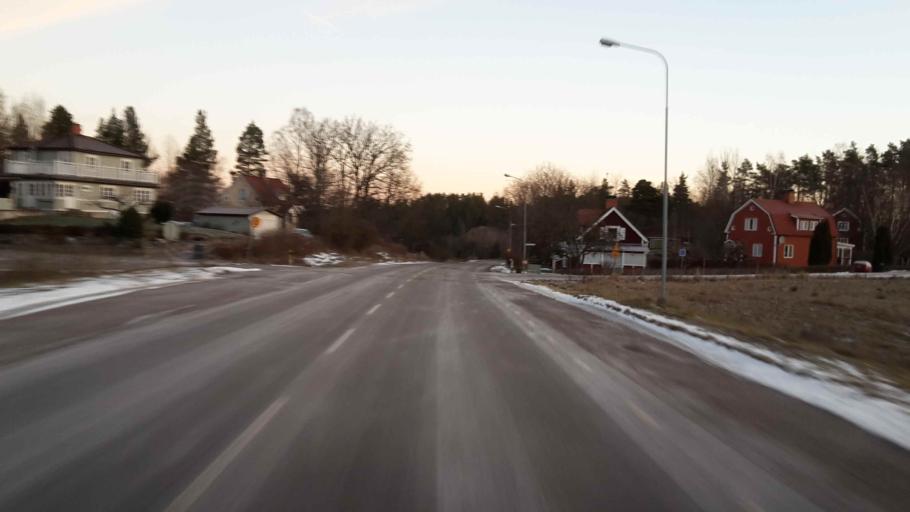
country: SE
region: OEstergoetland
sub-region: Atvidabergs Kommun
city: Atvidaberg
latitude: 58.2187
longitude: 16.0228
